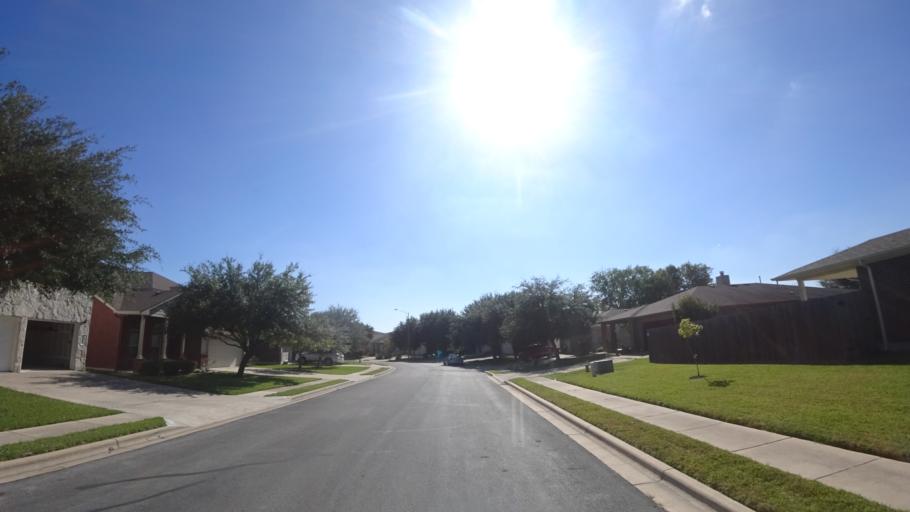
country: US
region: Texas
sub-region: Travis County
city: Manor
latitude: 30.3634
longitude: -97.6107
